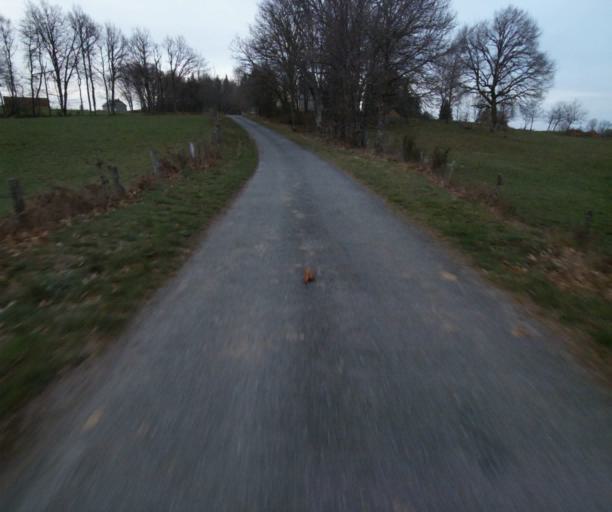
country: FR
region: Limousin
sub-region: Departement de la Correze
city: Correze
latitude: 45.4405
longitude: 1.8388
